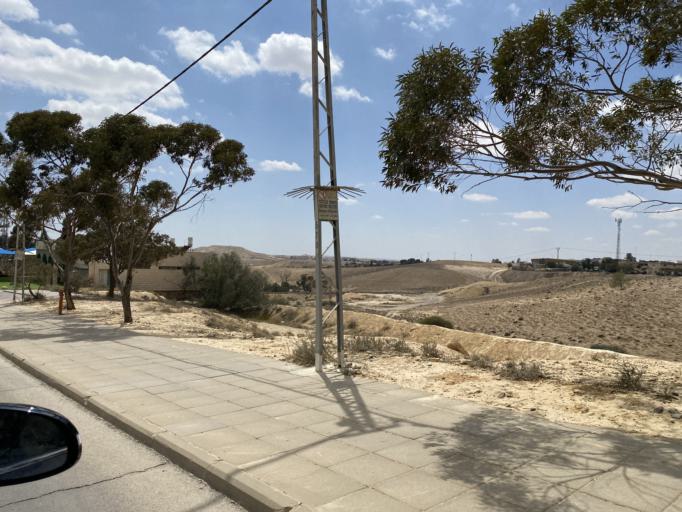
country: IL
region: Southern District
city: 'Arad
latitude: 31.2550
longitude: 35.2148
